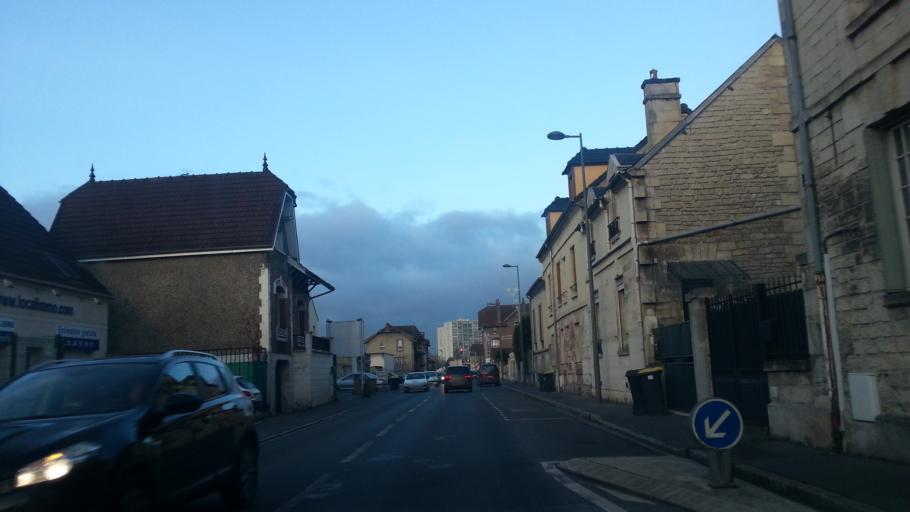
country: FR
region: Picardie
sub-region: Departement de l'Oise
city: Thiverny
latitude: 49.2552
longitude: 2.4371
